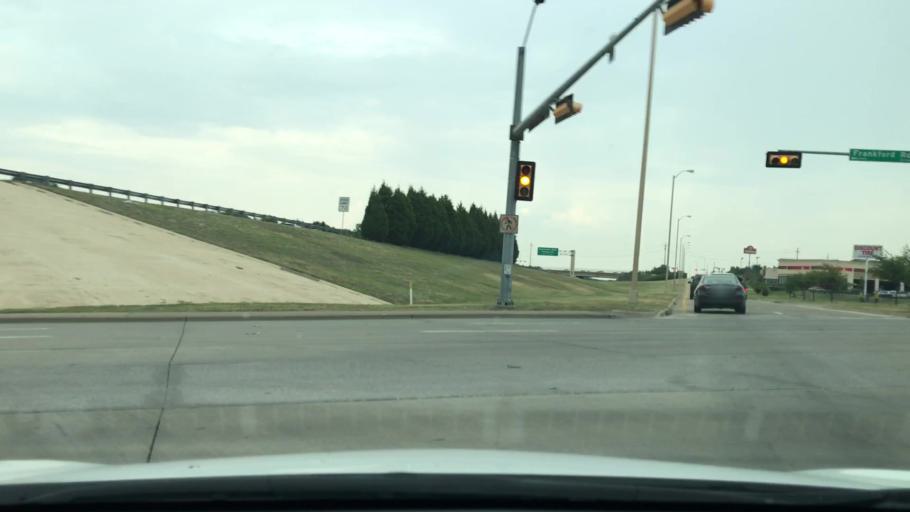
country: US
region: Texas
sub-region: Dallas County
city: Addison
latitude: 32.9969
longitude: -96.8587
